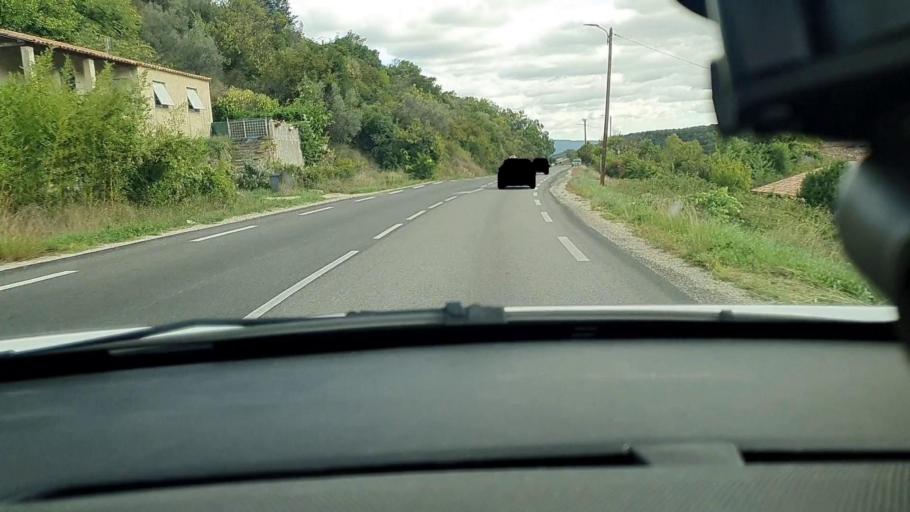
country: FR
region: Languedoc-Roussillon
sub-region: Departement du Gard
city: Les Mages
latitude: 44.2339
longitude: 4.1427
